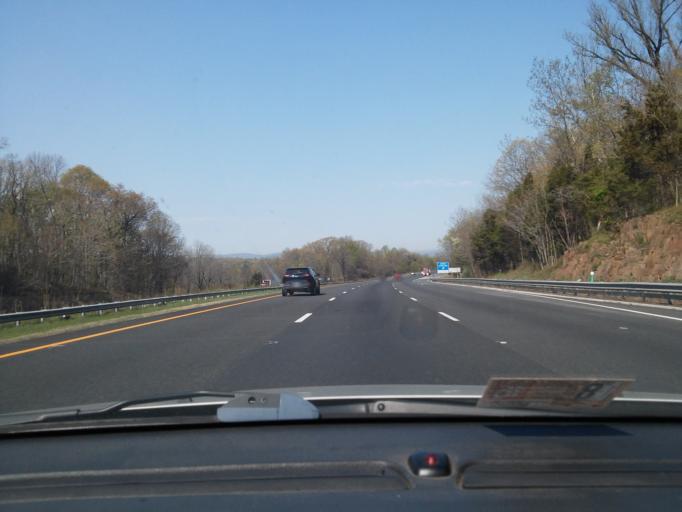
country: US
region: New Jersey
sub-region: Somerset County
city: Green Knoll
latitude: 40.6426
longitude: -74.6124
